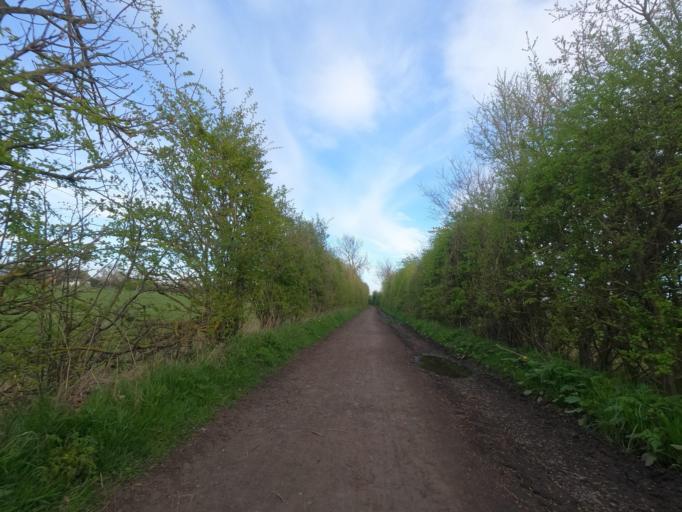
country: GB
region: England
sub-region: Newcastle upon Tyne
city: Hazlerigg
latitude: 55.0585
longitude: -1.6446
